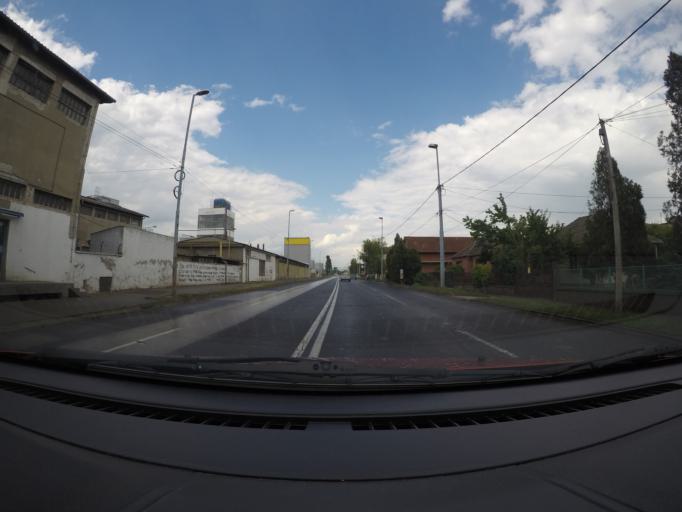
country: RS
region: Autonomna Pokrajina Vojvodina
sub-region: Srednjebanatski Okrug
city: Zrenjanin
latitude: 45.3851
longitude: 20.4184
